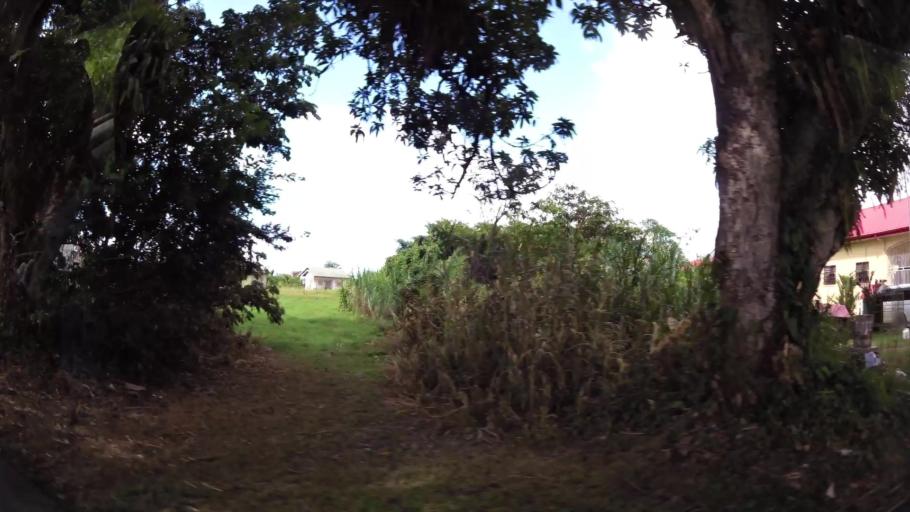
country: SR
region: Paramaribo
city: Paramaribo
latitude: 5.8518
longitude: -55.1603
